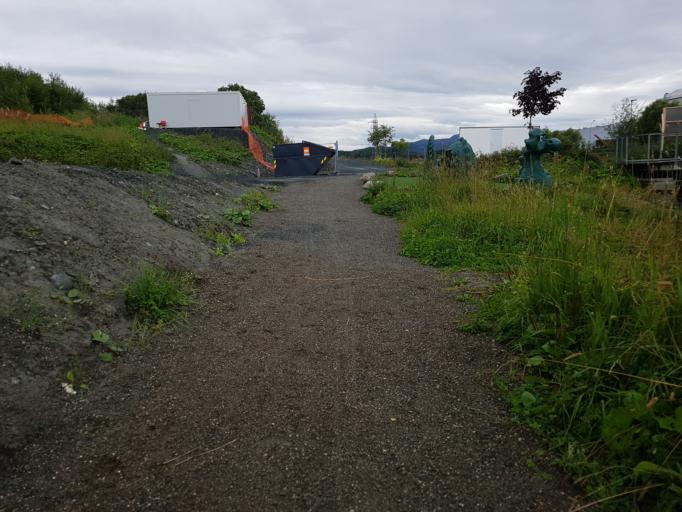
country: NO
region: Sor-Trondelag
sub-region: Trondheim
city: Trondheim
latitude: 63.3890
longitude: 10.4355
